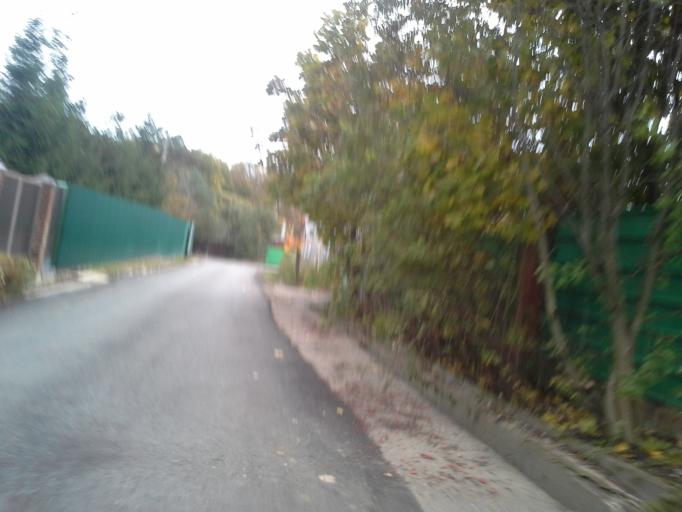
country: RU
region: Moskovskaya
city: Kokoshkino
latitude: 55.6176
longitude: 37.1643
